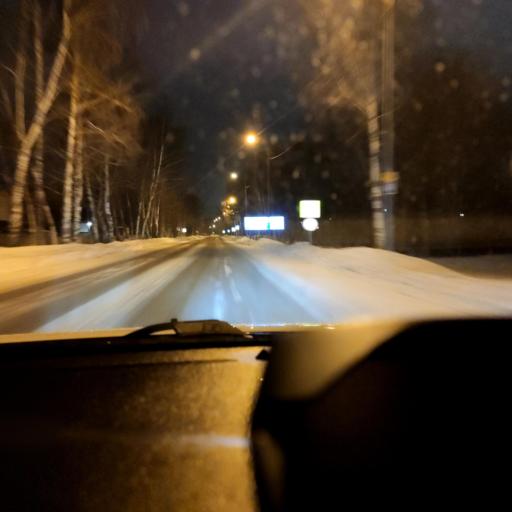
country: RU
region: Tatarstan
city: Vysokaya Gora
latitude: 55.8891
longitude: 49.2445
